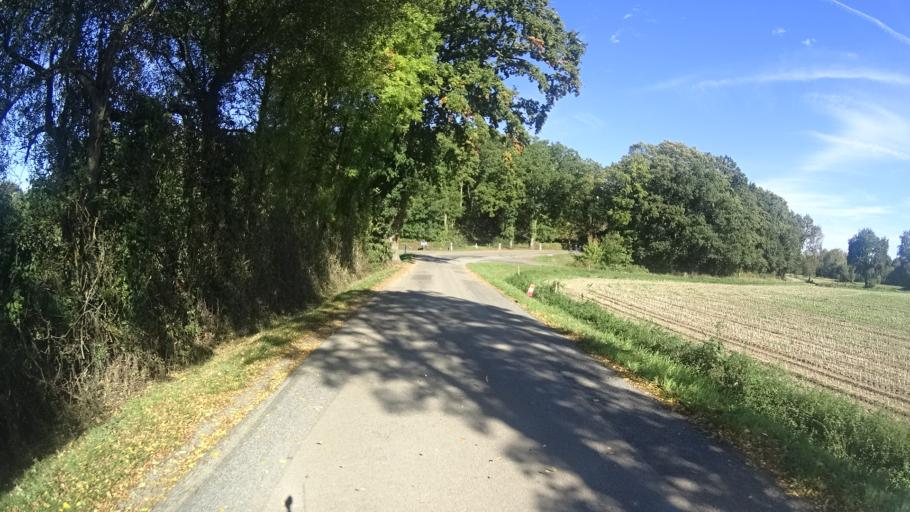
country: FR
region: Brittany
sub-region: Departement du Morbihan
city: Saint-Vincent-sur-Oust
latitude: 47.7248
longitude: -2.1640
